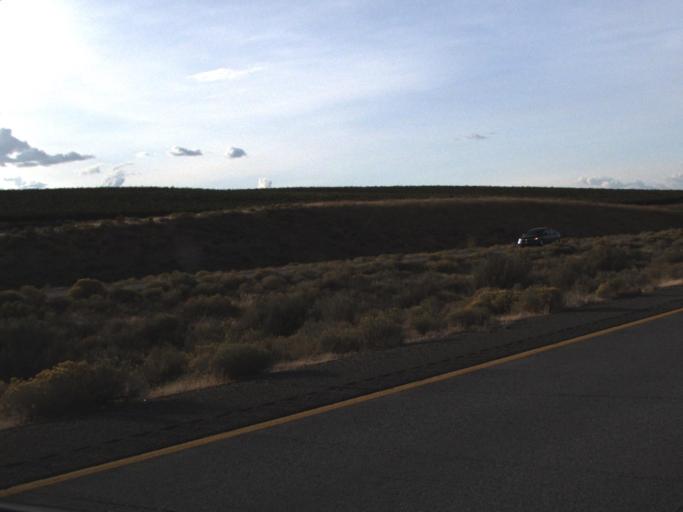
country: US
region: Washington
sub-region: Benton County
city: West Richland
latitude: 46.2189
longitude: -119.3486
